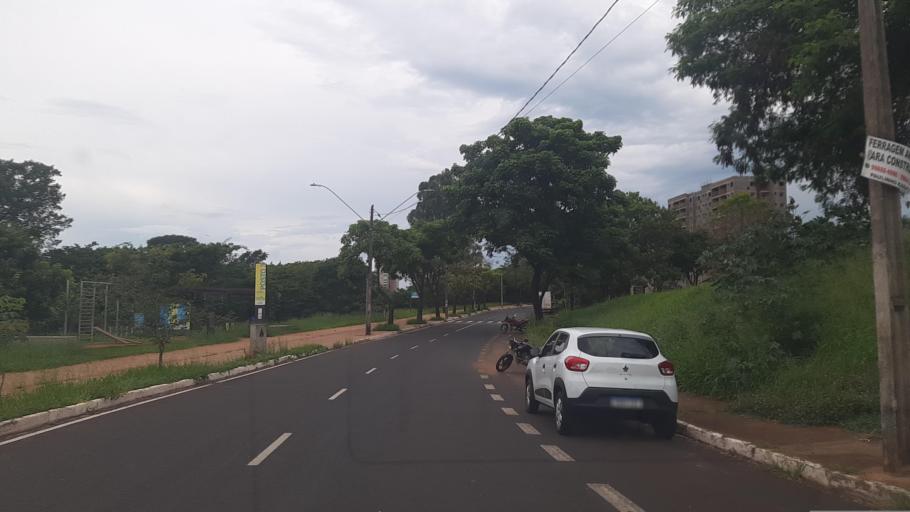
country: BR
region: Minas Gerais
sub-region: Uberlandia
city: Uberlandia
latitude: -18.9241
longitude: -48.2993
